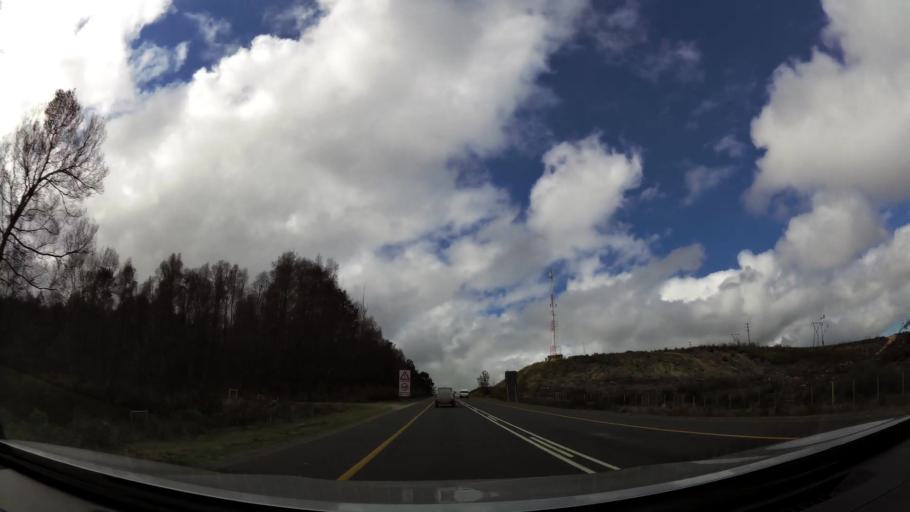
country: ZA
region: Western Cape
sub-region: Eden District Municipality
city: Knysna
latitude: -34.0374
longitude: 23.1433
